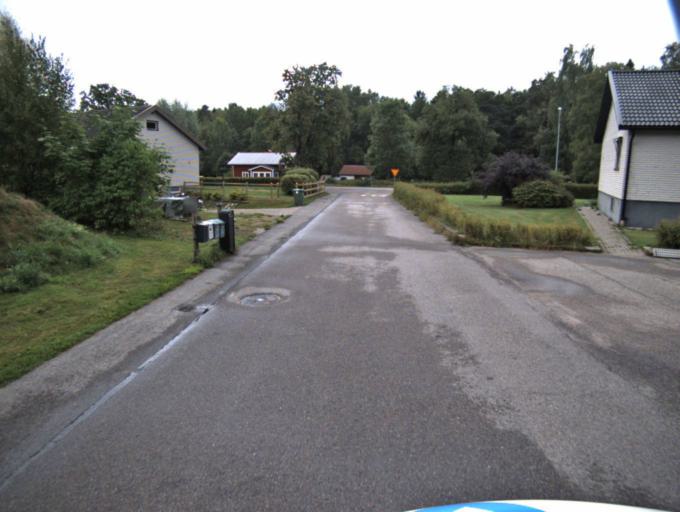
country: SE
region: Vaestra Goetaland
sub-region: Tranemo Kommun
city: Langhem
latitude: 57.6990
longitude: 13.3003
